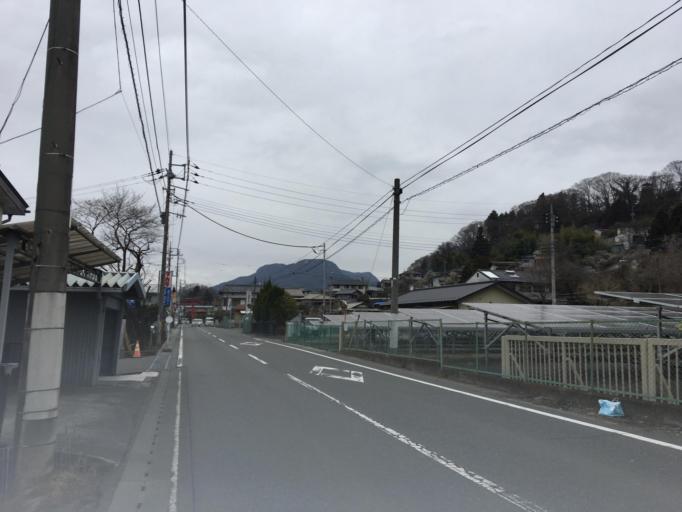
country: JP
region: Gunma
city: Numata
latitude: 36.6450
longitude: 139.0371
